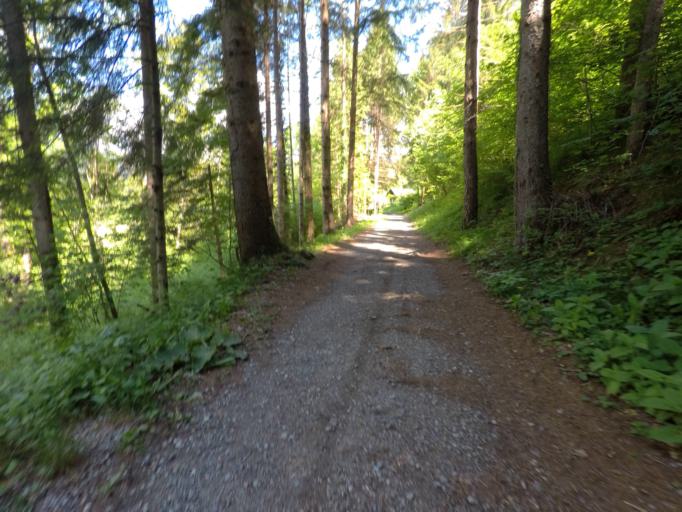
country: IT
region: Friuli Venezia Giulia
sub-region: Provincia di Udine
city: Ovaro
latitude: 46.4772
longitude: 12.8715
